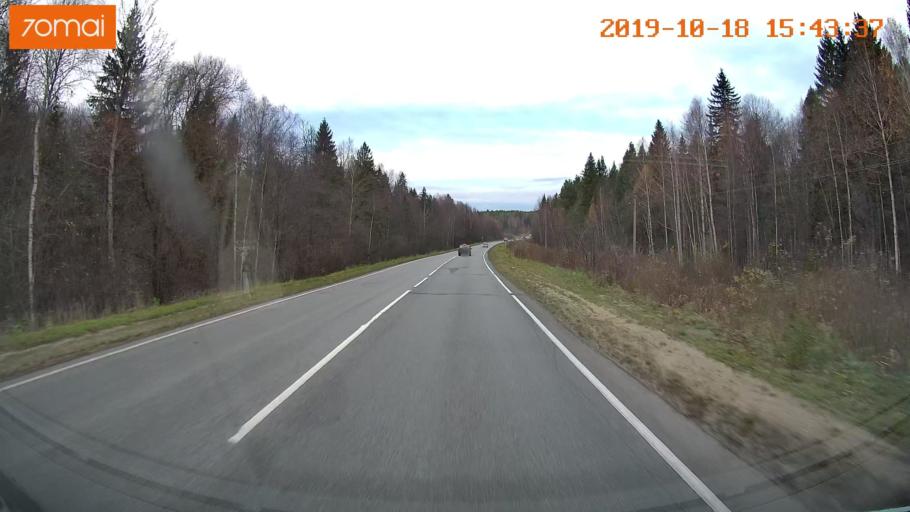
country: RU
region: Vladimir
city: Golovino
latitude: 55.9703
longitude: 40.5490
